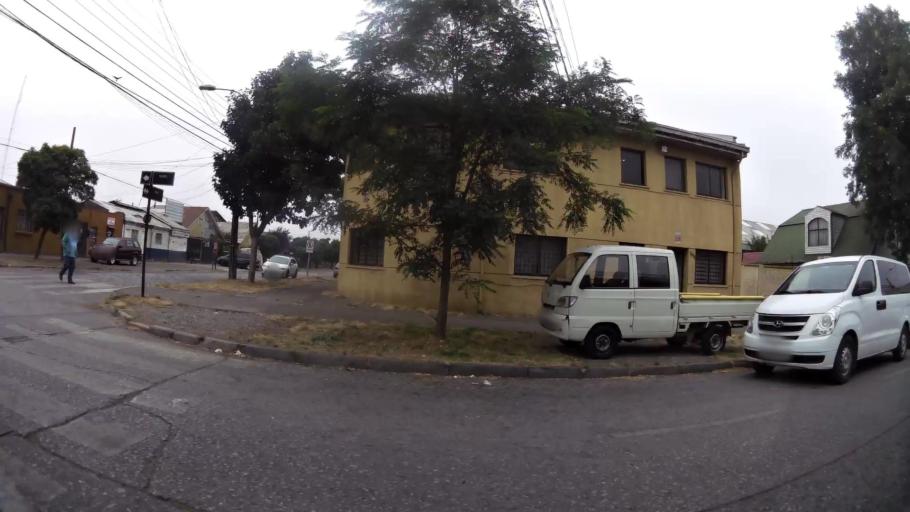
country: CL
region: Biobio
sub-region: Provincia de Concepcion
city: Concepcion
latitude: -36.8124
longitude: -73.0540
